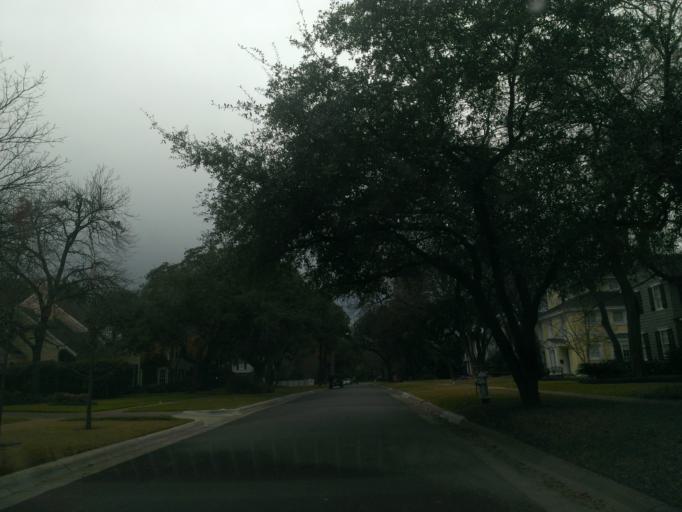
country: US
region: Texas
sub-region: Travis County
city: Austin
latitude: 30.2929
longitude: -97.7574
